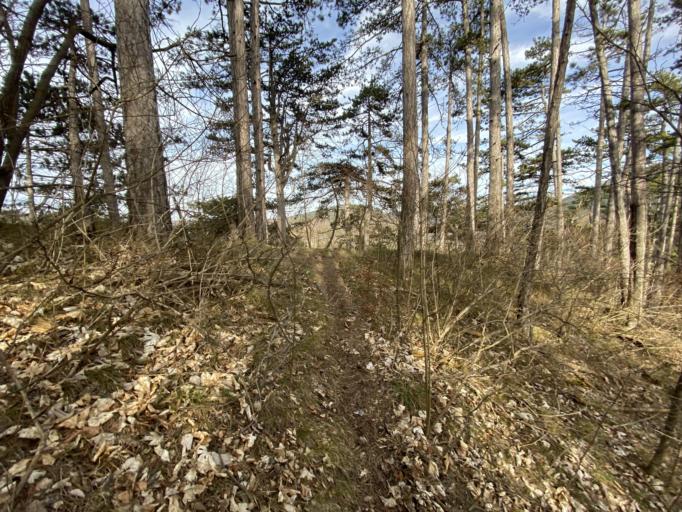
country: AT
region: Lower Austria
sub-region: Politischer Bezirk Modling
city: Gaaden
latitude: 48.0108
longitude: 16.1630
